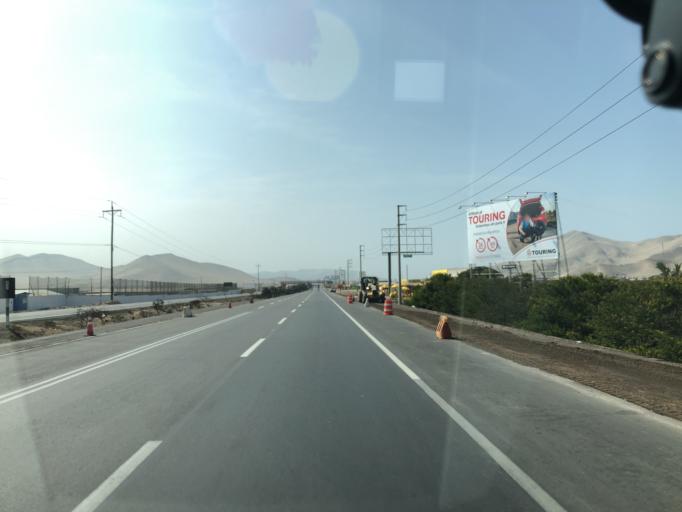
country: PE
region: Lima
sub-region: Provincia de Canete
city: Chilca
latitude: -12.5360
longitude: -76.7199
